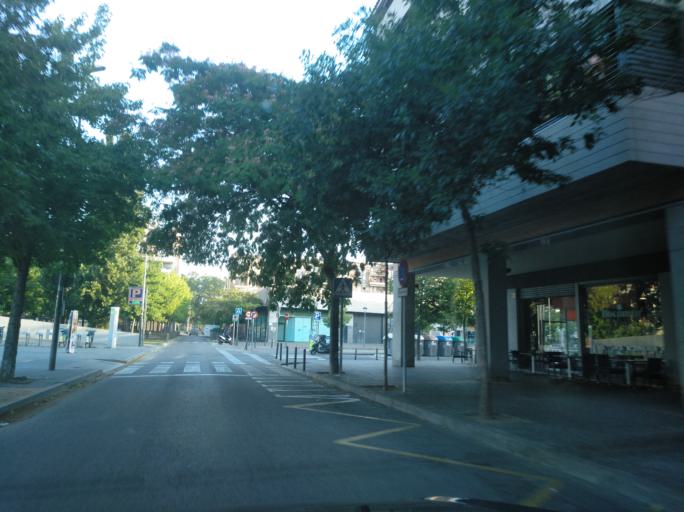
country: ES
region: Catalonia
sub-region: Provincia de Girona
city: Girona
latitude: 41.9823
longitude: 2.8149
